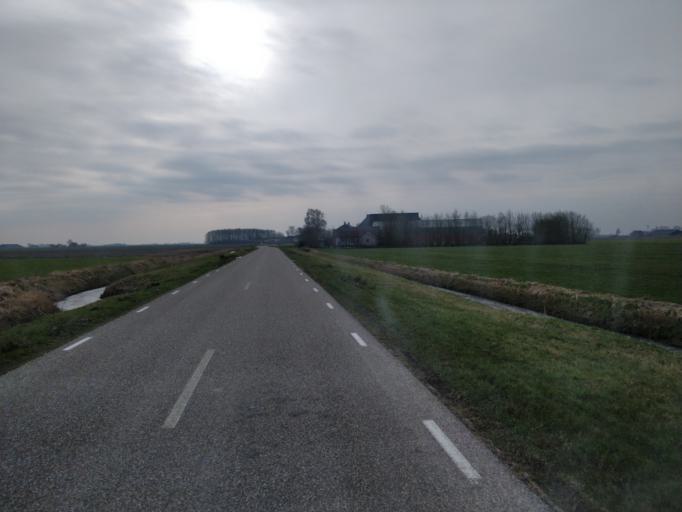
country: NL
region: Friesland
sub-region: Gemeente Dongeradeel
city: Ternaard
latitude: 53.3576
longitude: 5.9381
